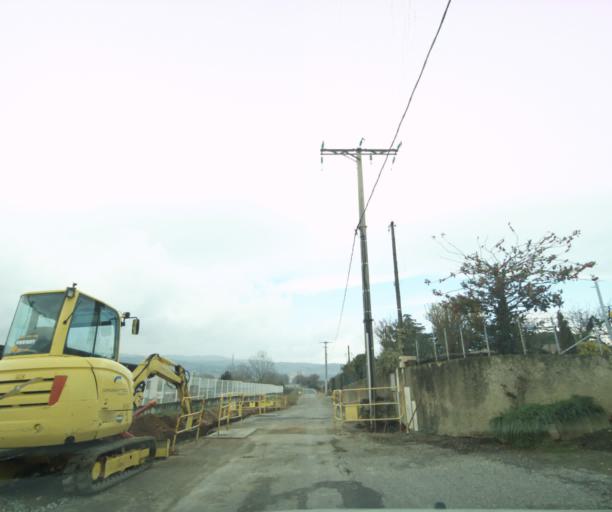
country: FR
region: Rhone-Alpes
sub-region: Departement de l'Ardeche
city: Cornas
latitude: 44.9687
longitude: 4.8795
